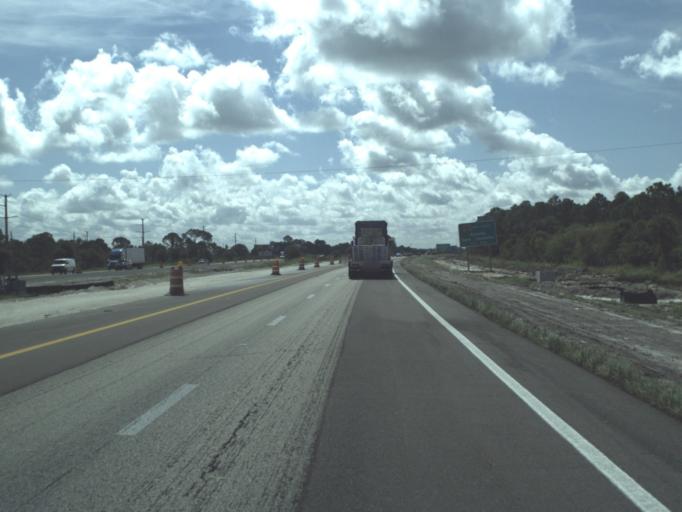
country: US
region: Florida
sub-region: Charlotte County
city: Port Charlotte
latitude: 27.0395
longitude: -82.0625
